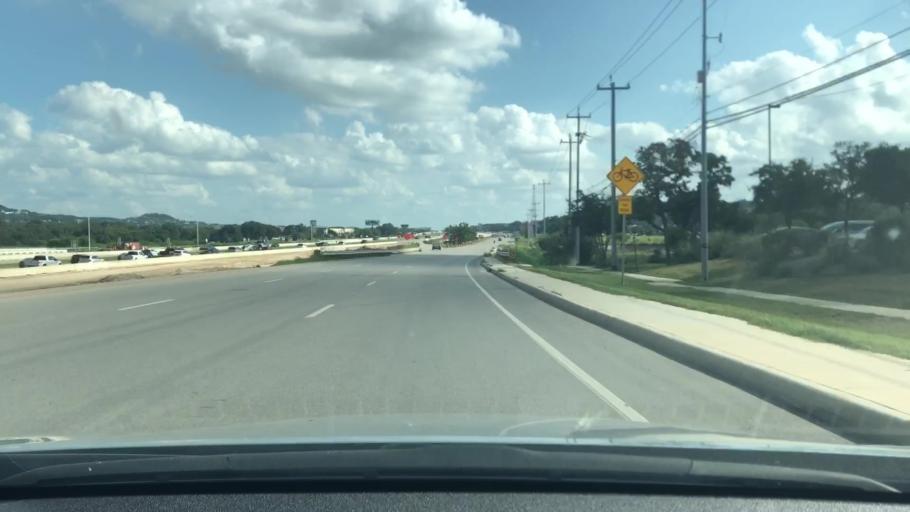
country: US
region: Texas
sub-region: Bexar County
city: Cross Mountain
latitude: 29.6739
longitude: -98.6357
